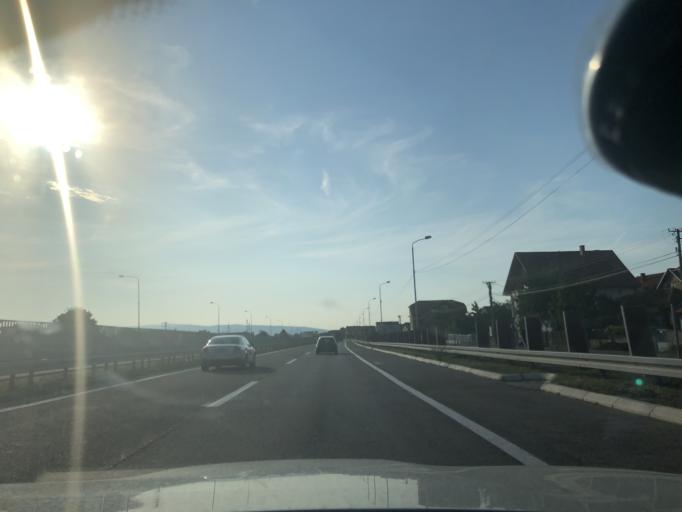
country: RS
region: Central Serbia
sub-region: Nisavski Okrug
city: Nis
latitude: 43.3431
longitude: 21.8824
